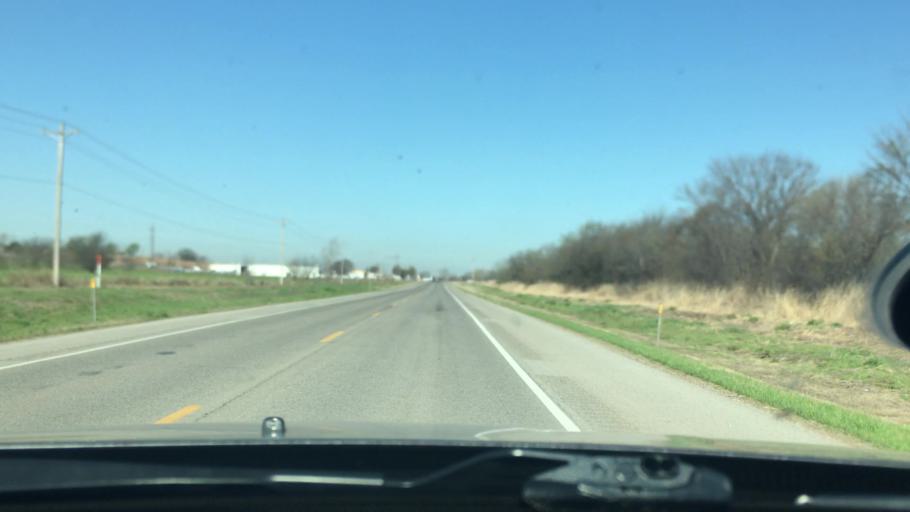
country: US
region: Oklahoma
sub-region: Garvin County
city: Lindsay
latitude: 34.8273
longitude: -97.5587
